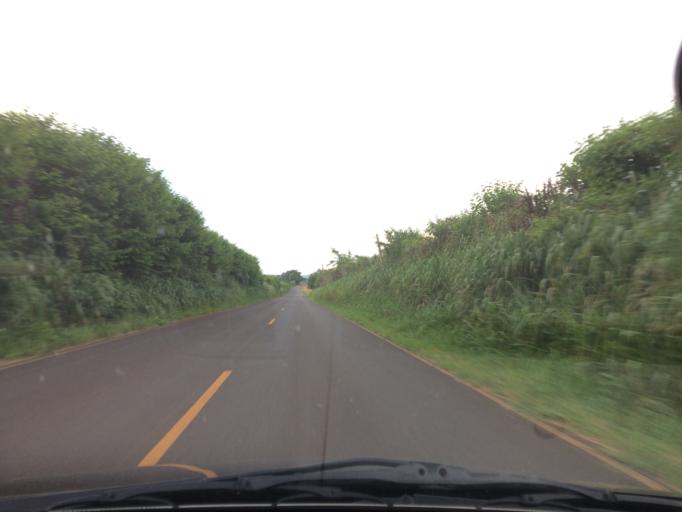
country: BR
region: Sao Paulo
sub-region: Casa Branca
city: Casa Branca
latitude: -21.7588
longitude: -47.1132
